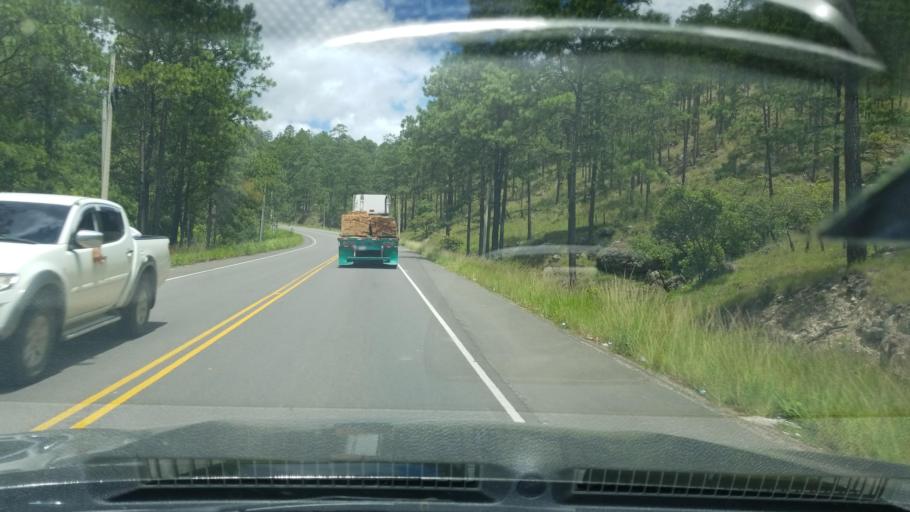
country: HN
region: Francisco Morazan
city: Talanga
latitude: 14.3978
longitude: -87.1266
